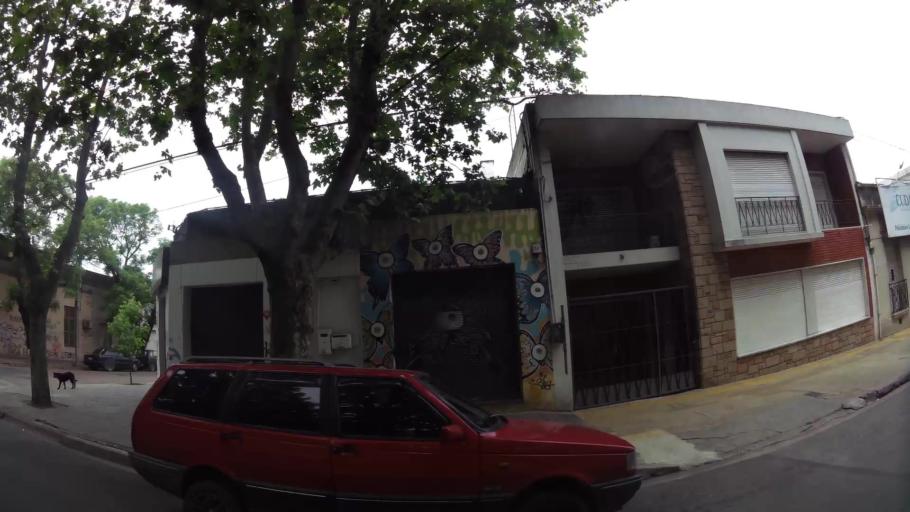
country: UY
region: Canelones
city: Las Piedras
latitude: -34.7281
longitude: -56.2184
